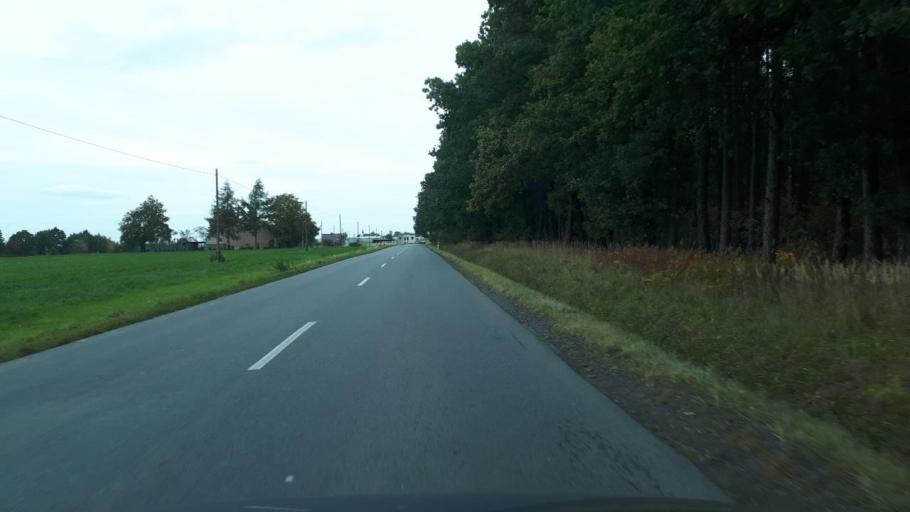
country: PL
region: Opole Voivodeship
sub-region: Powiat oleski
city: Dobrodzien
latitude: 50.7070
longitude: 18.4453
